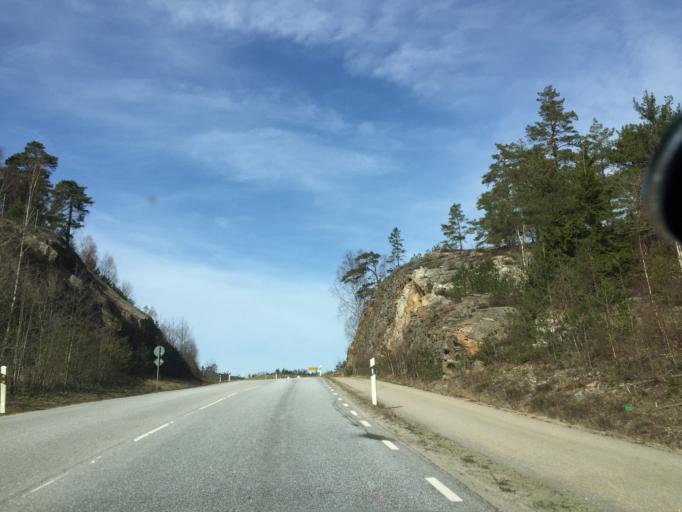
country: SE
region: Vaestra Goetaland
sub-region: Uddevalla Kommun
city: Uddevalla
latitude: 58.3617
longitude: 11.8077
